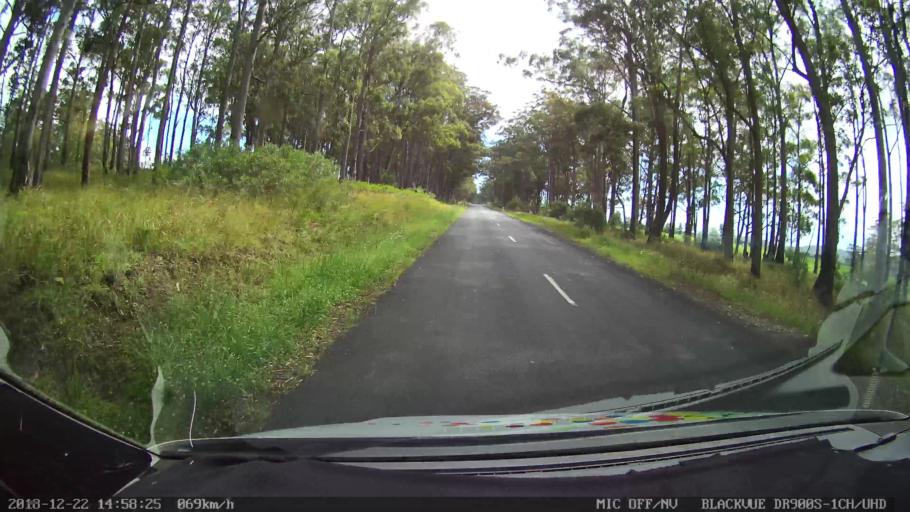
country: AU
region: New South Wales
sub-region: Bellingen
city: Dorrigo
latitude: -30.2400
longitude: 152.4913
